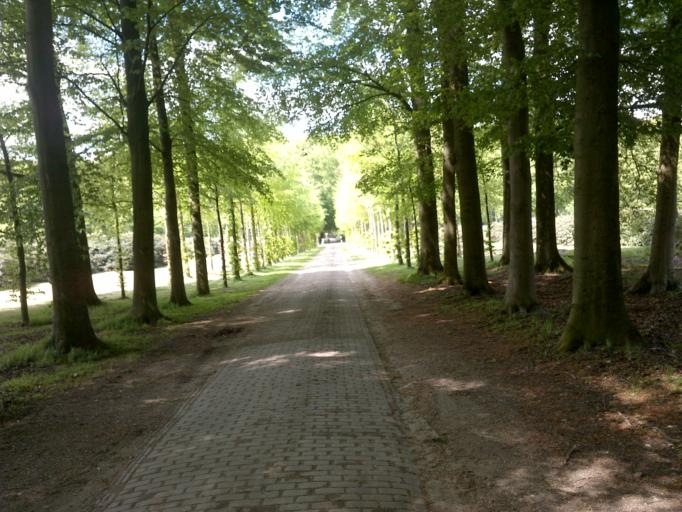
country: NL
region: Gelderland
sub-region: Gemeente Rheden
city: De Steeg
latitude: 52.0215
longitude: 6.0693
